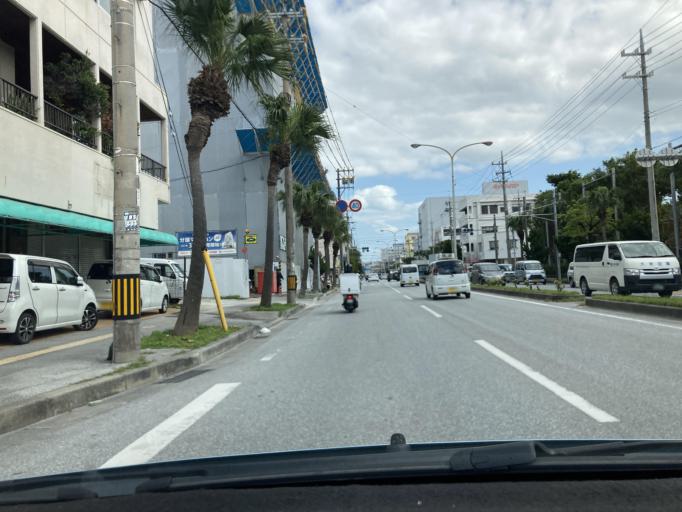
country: JP
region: Okinawa
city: Naha-shi
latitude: 26.2413
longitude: 127.6825
